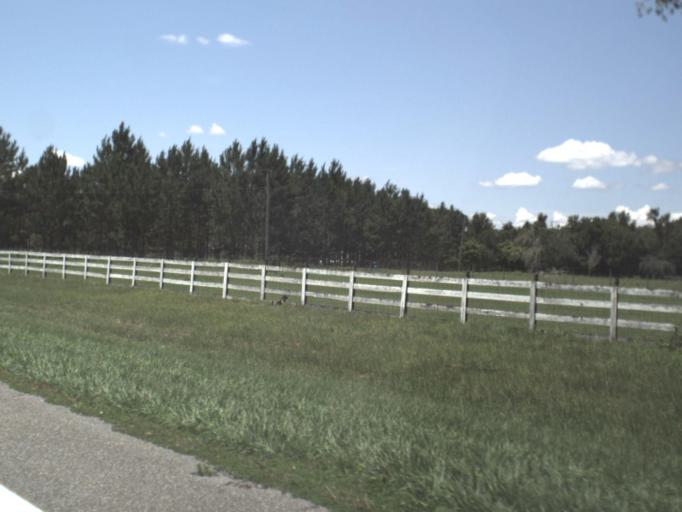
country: US
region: Florida
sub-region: Lafayette County
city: Mayo
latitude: 30.0509
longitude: -83.0867
